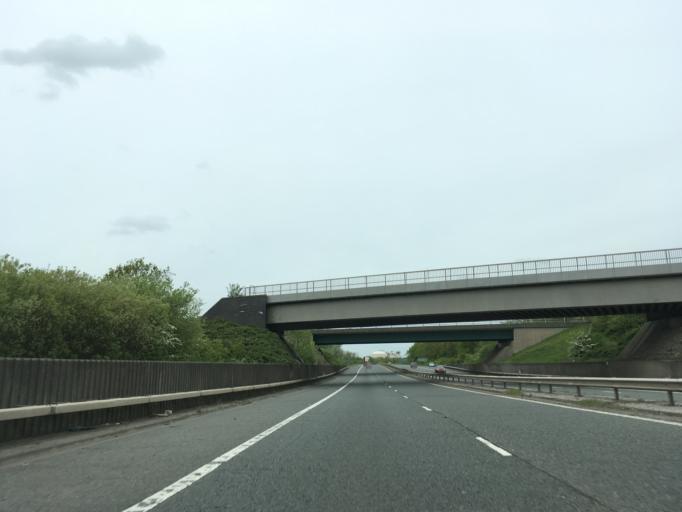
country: GB
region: England
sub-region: South Gloucestershire
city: Severn Beach
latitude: 51.5164
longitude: -2.6618
